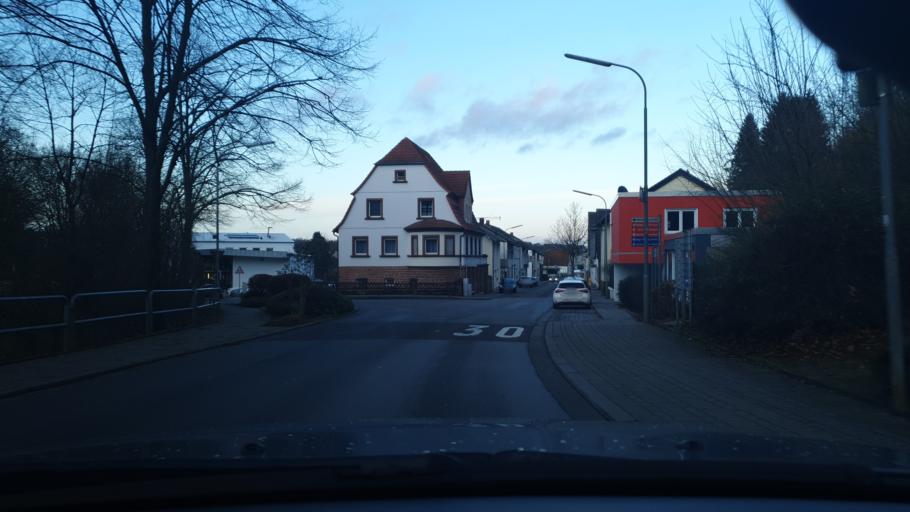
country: DE
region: Rheinland-Pfalz
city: Stelzenberg
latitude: 49.4157
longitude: 7.6986
